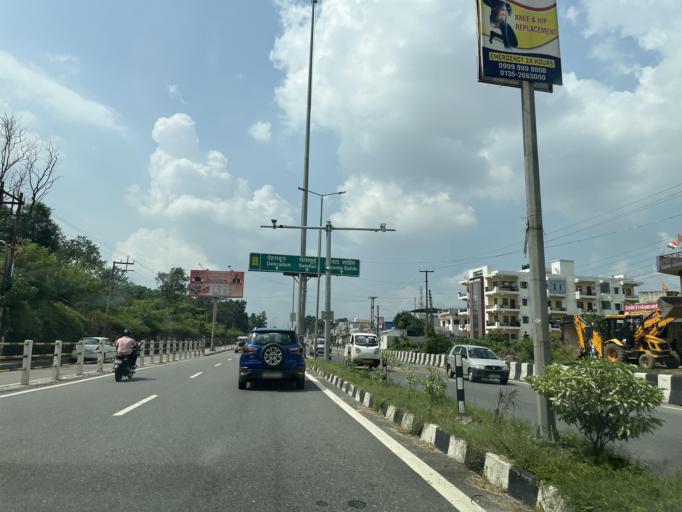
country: IN
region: Uttarakhand
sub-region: Dehradun
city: Raipur
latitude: 30.2727
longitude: 78.0779
